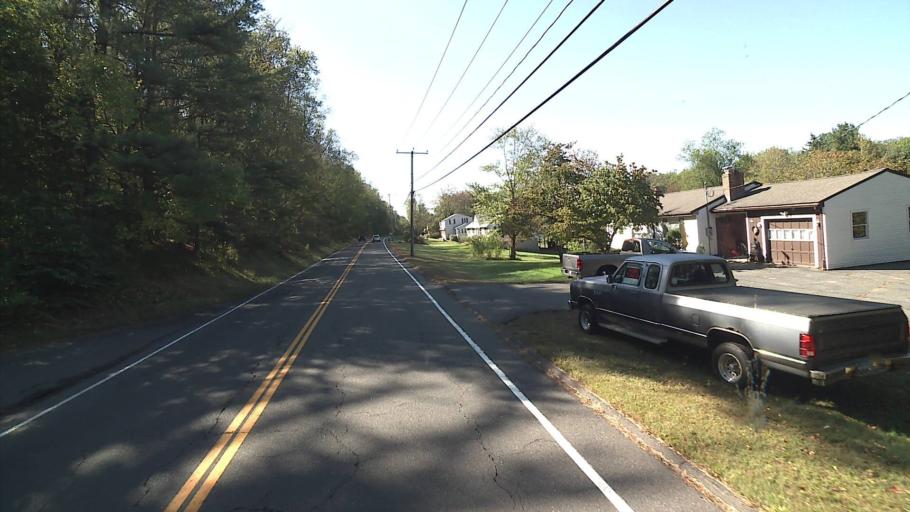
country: US
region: Connecticut
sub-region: Tolland County
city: Ellington
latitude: 41.9409
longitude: -72.4509
